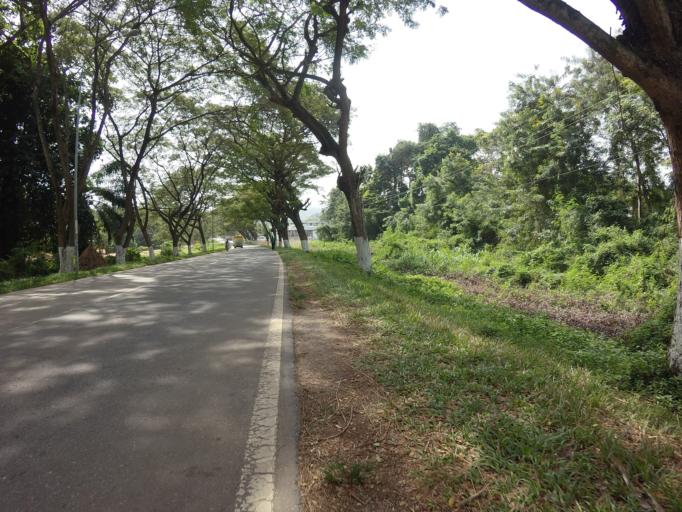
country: GH
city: Akropong
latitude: 6.2771
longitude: 0.0525
